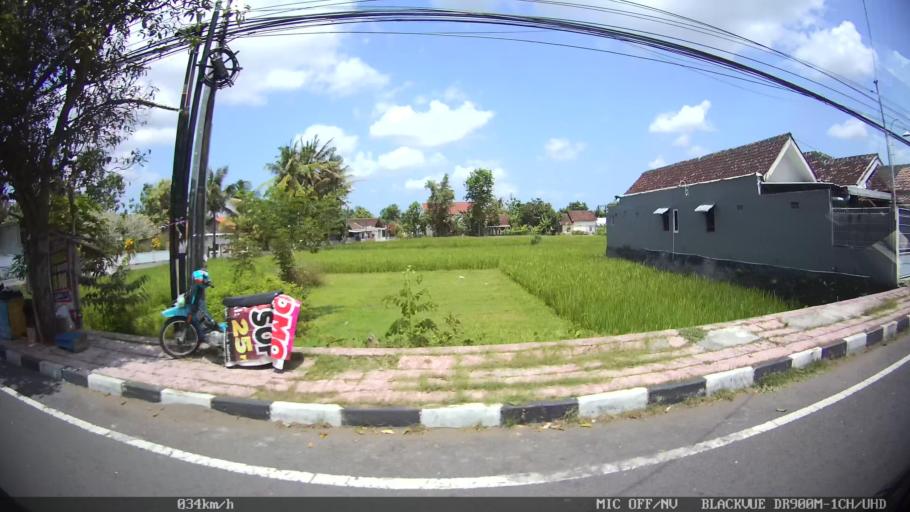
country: ID
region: Daerah Istimewa Yogyakarta
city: Bantul
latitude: -7.8943
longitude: 110.3438
